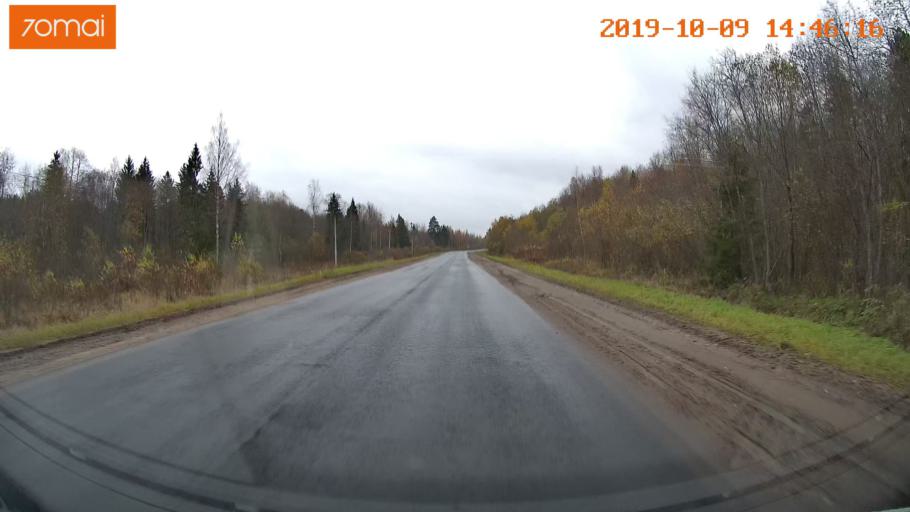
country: RU
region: Kostroma
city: Buy
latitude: 58.4336
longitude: 41.5770
